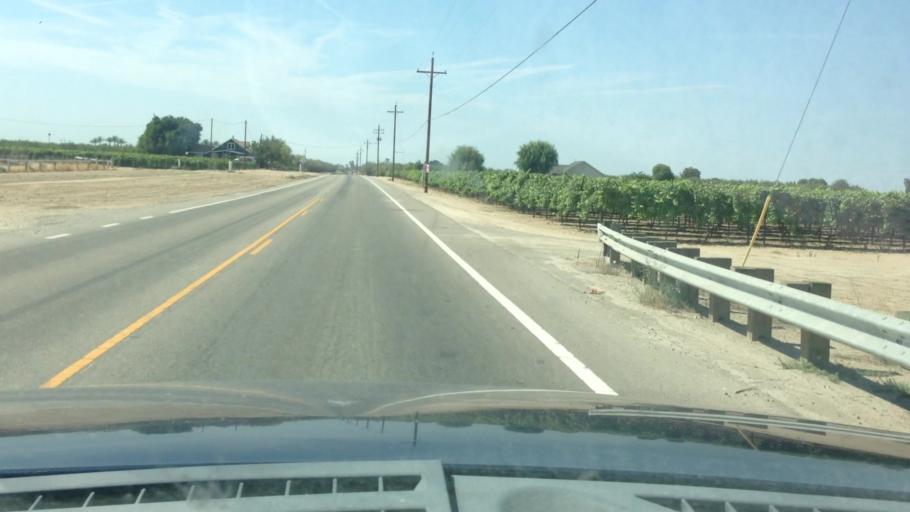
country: US
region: California
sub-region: Fresno County
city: Parlier
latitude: 36.5901
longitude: -119.5571
